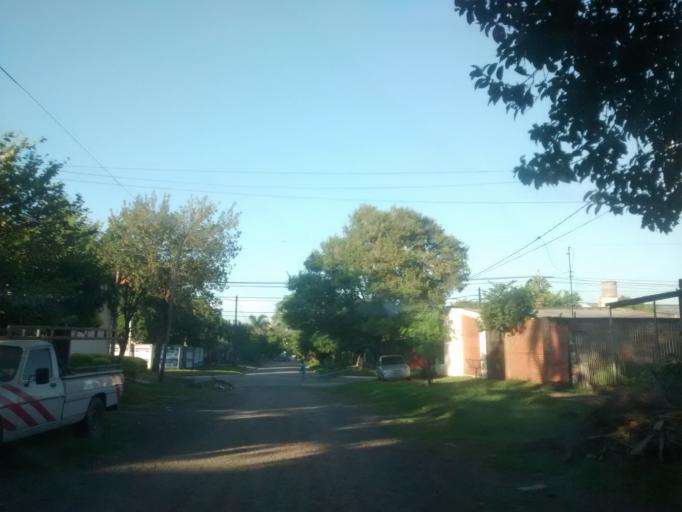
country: AR
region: Chaco
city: Resistencia
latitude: -27.4430
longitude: -58.9739
